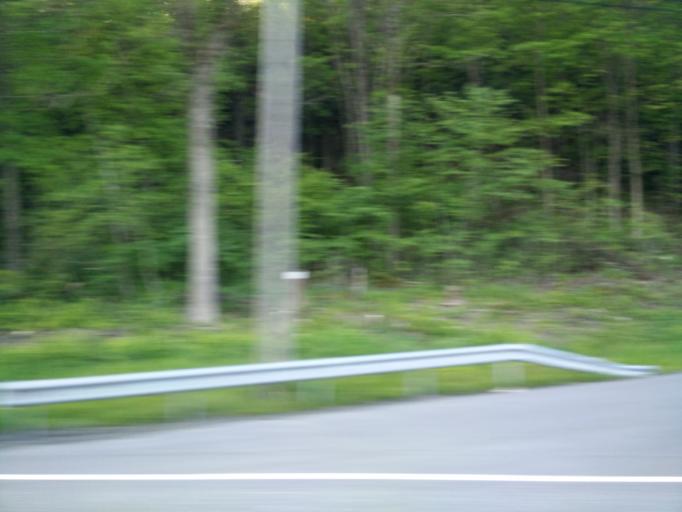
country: NO
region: Akershus
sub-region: Baerum
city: Skui
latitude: 59.9395
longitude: 10.4080
